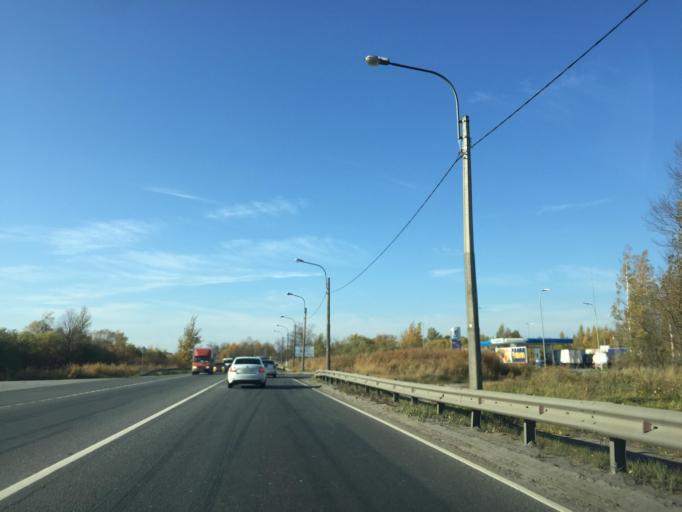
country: RU
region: St.-Petersburg
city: Petro-Slavyanka
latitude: 59.7475
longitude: 30.5102
